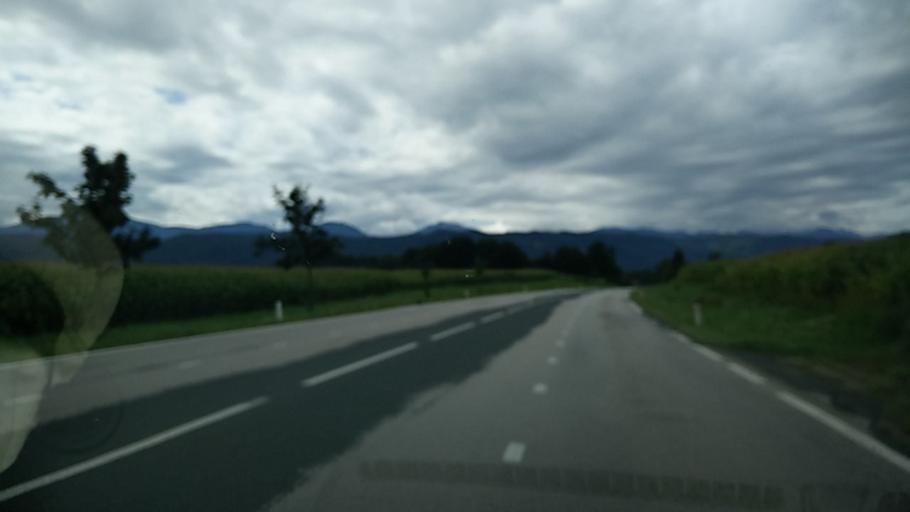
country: AT
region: Carinthia
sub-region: Politischer Bezirk Klagenfurt Land
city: Poggersdorf
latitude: 46.6369
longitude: 14.4226
